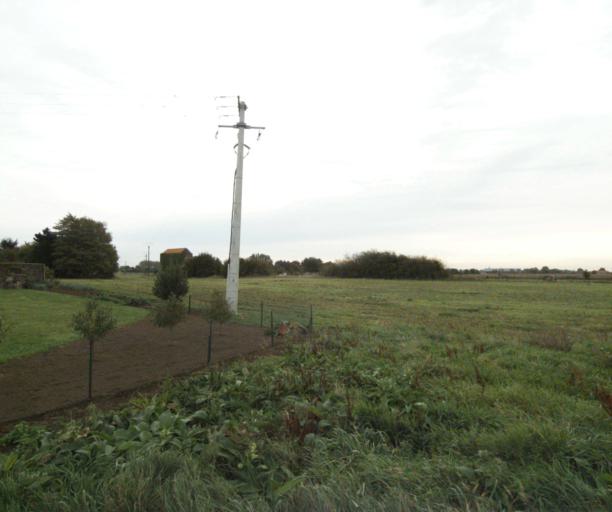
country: FR
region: Nord-Pas-de-Calais
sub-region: Departement du Nord
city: Aubers
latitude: 50.5934
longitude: 2.8258
